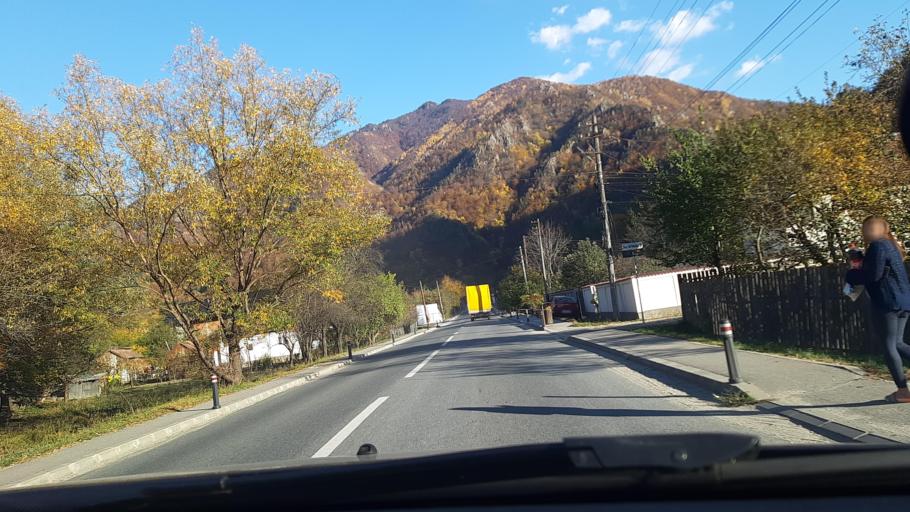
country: RO
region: Valcea
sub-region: Comuna Brezoi
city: Brezoi
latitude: 45.3334
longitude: 24.2708
